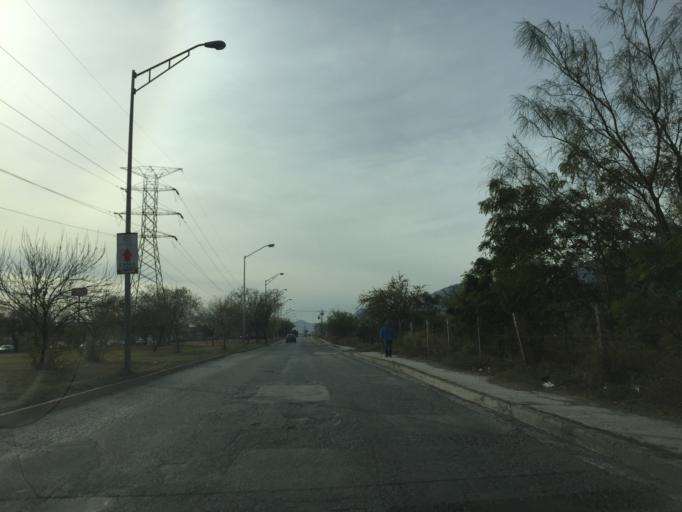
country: MX
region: Nuevo Leon
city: Guadalupe
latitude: 25.7010
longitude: -100.2145
